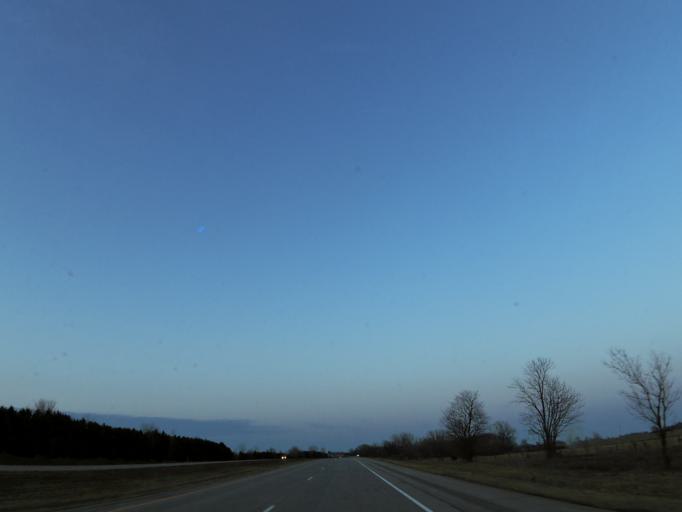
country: US
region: Minnesota
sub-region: Mower County
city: Grand Meadow
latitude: 43.6913
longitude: -92.7283
